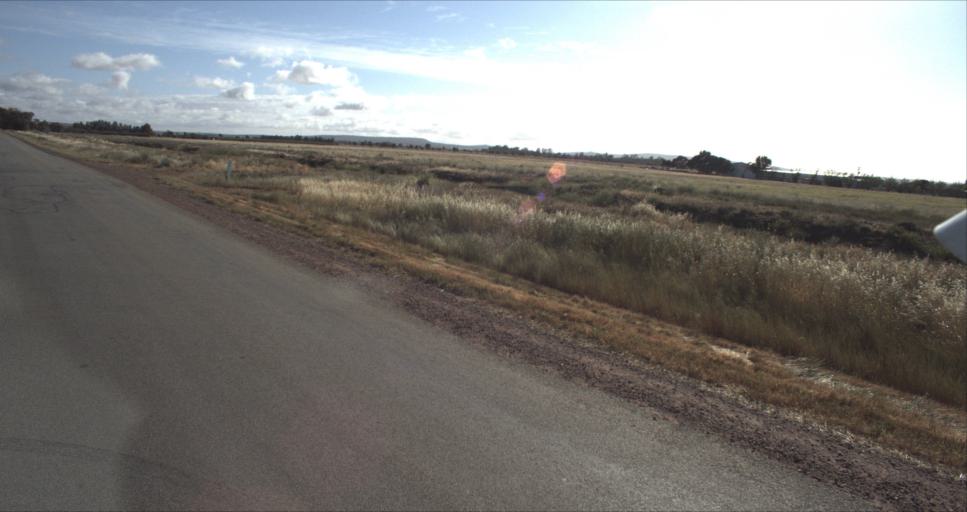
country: AU
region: New South Wales
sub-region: Leeton
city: Leeton
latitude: -34.5261
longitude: 146.3896
